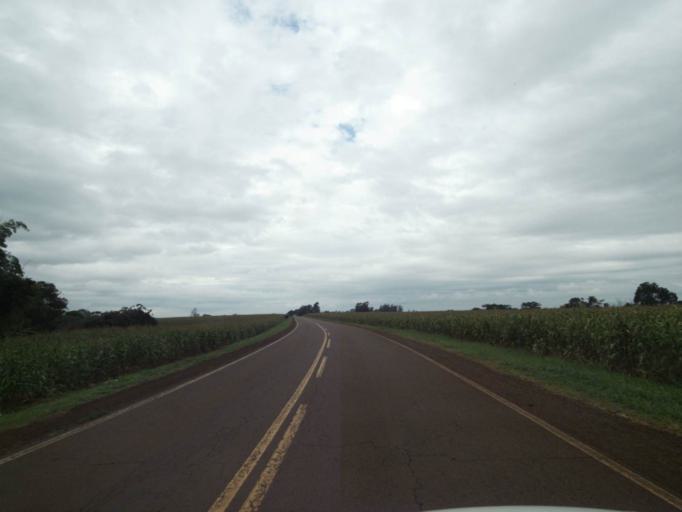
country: BR
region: Parana
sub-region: Marechal Candido Rondon
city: Marechal Candido Rondon
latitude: -24.8184
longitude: -54.1854
